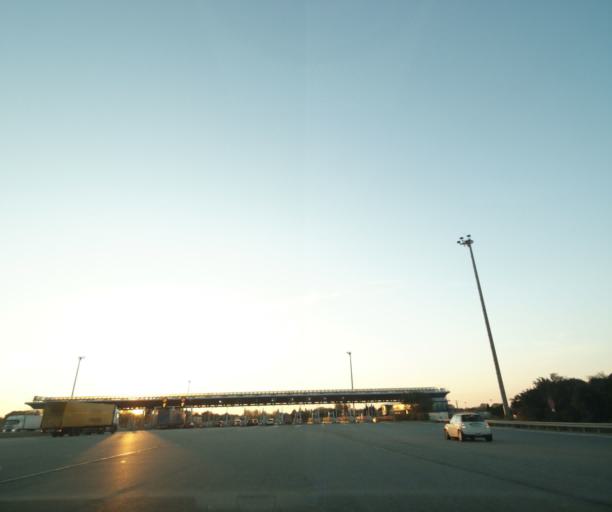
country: FR
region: Provence-Alpes-Cote d'Azur
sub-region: Departement des Bouches-du-Rhone
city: Saint-Martin-de-Crau
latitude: 43.6382
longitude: 4.8593
